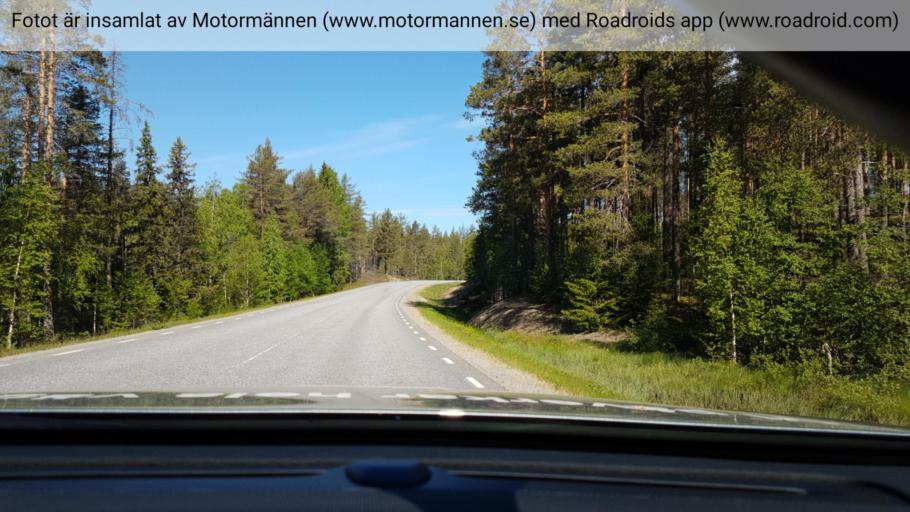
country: SE
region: Vaesterbotten
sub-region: Bjurholms Kommun
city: Bjurholm
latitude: 63.9747
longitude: 18.8190
